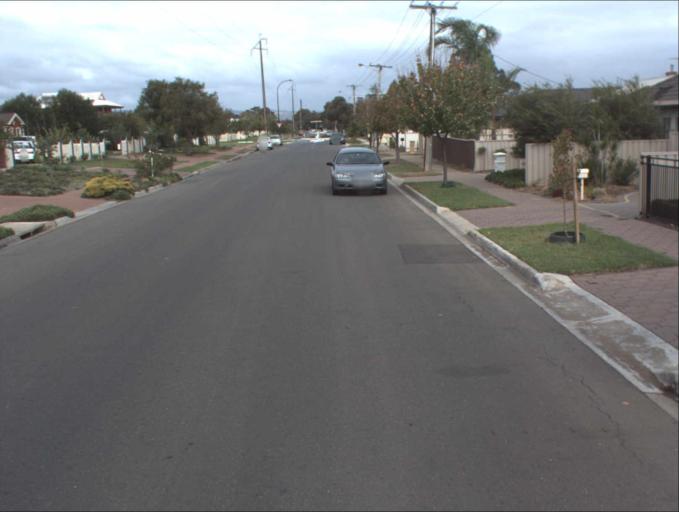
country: AU
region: South Australia
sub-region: Salisbury
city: Ingle Farm
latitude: -34.8535
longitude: 138.6267
